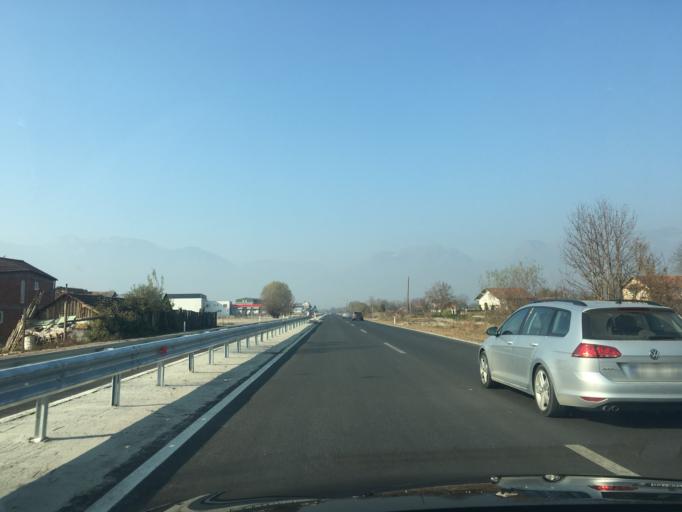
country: XK
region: Pec
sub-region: Komuna e Pejes
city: Dubova (Driloni)
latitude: 42.6587
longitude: 20.3790
